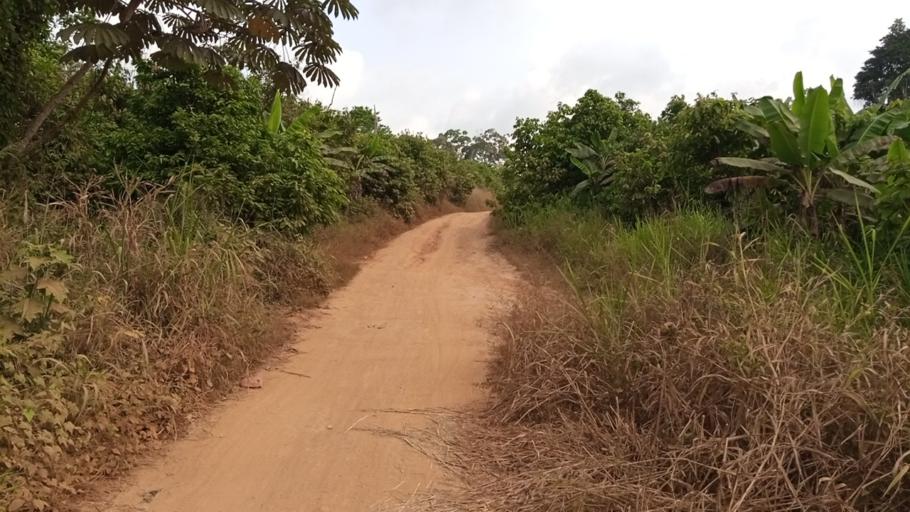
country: NG
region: Osun
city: Ifetedo
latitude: 7.0302
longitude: 4.5535
